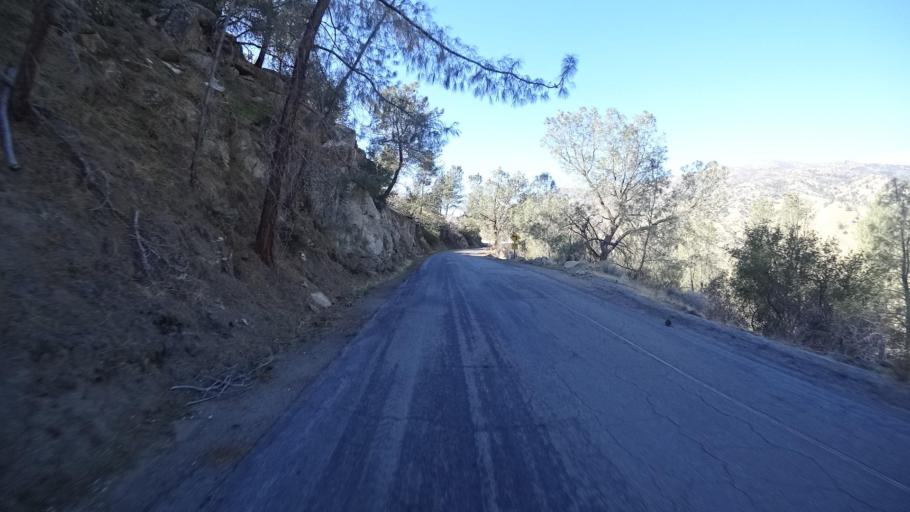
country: US
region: California
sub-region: Kern County
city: Bodfish
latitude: 35.5550
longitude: -118.6082
